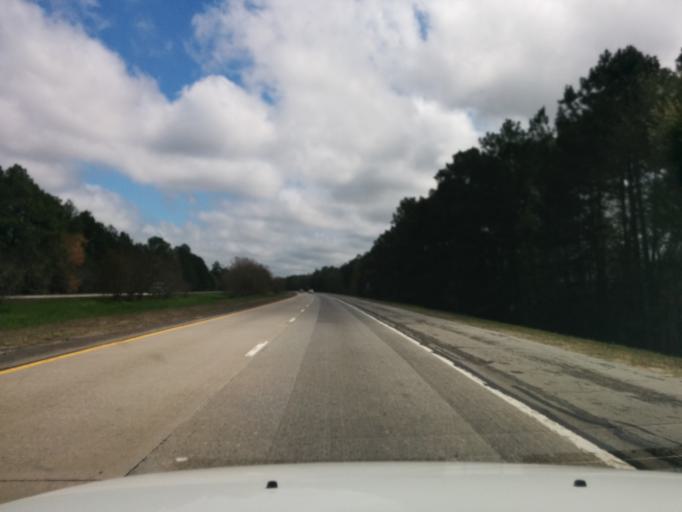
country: US
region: Georgia
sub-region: Chatham County
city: Bloomingdale
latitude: 32.1202
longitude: -81.3797
